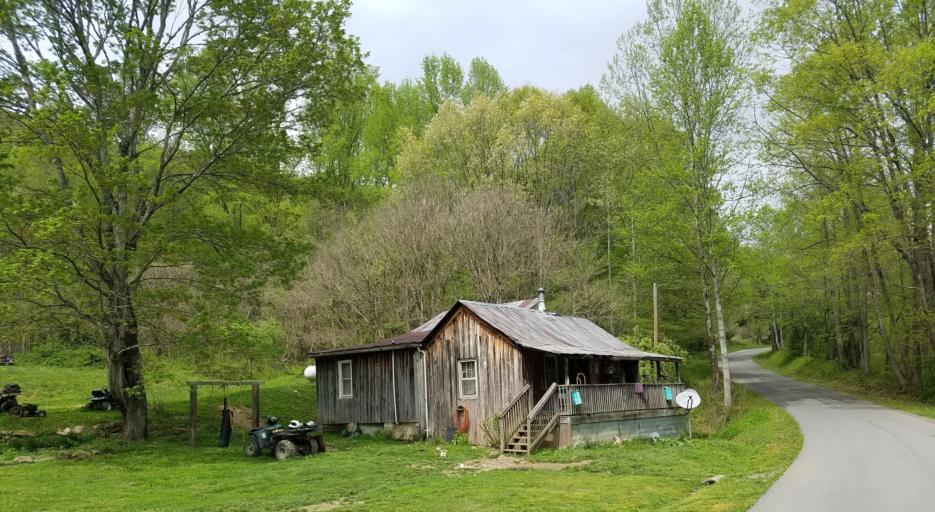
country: US
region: Kentucky
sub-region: Harlan County
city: Harlan
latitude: 36.7137
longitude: -83.2598
